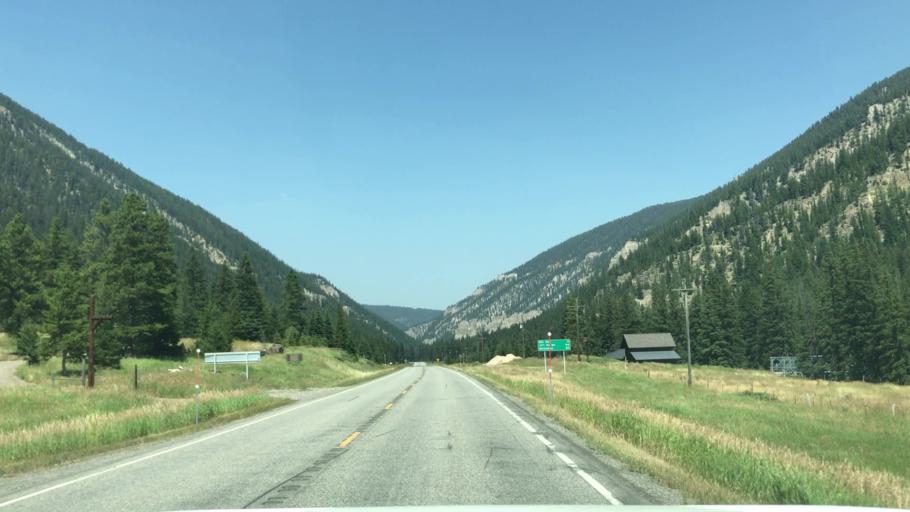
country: US
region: Montana
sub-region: Gallatin County
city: Big Sky
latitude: 45.1180
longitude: -111.2265
